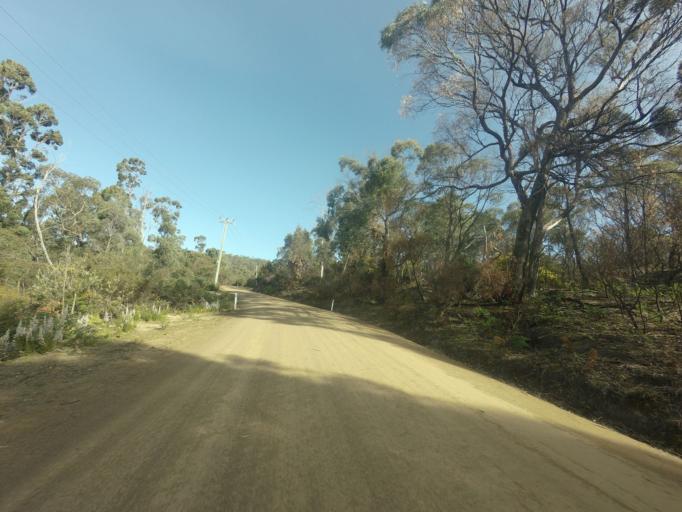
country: AU
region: Tasmania
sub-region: Kingborough
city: Margate
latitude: -43.0789
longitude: 147.2651
